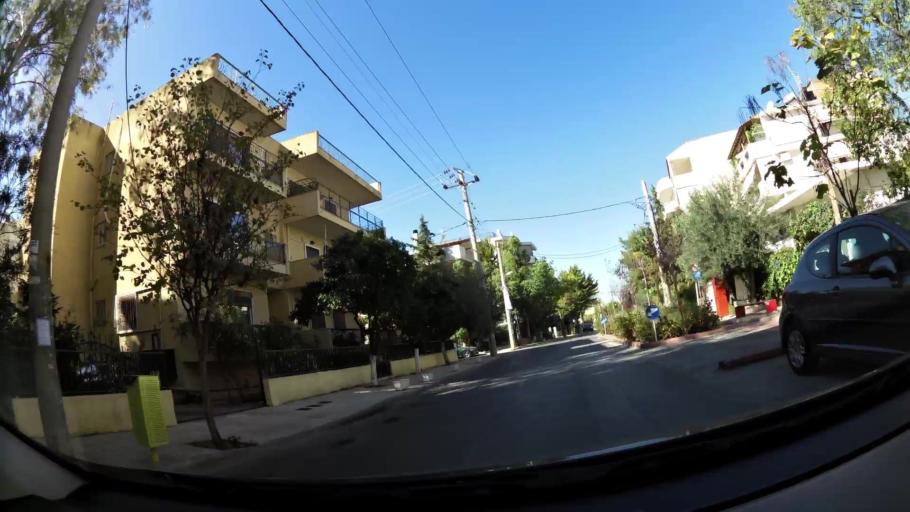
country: GR
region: Attica
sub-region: Nomarchia Athinas
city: Khalandrion
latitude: 38.0354
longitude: 23.8118
